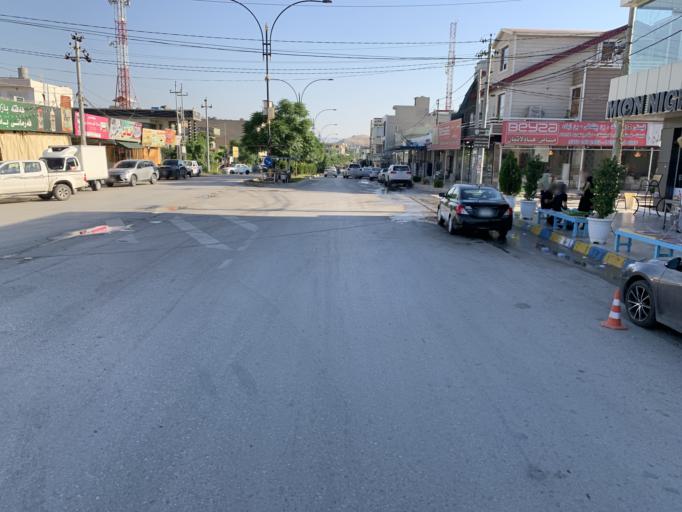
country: IQ
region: As Sulaymaniyah
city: Raniye
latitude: 36.2491
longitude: 44.8759
